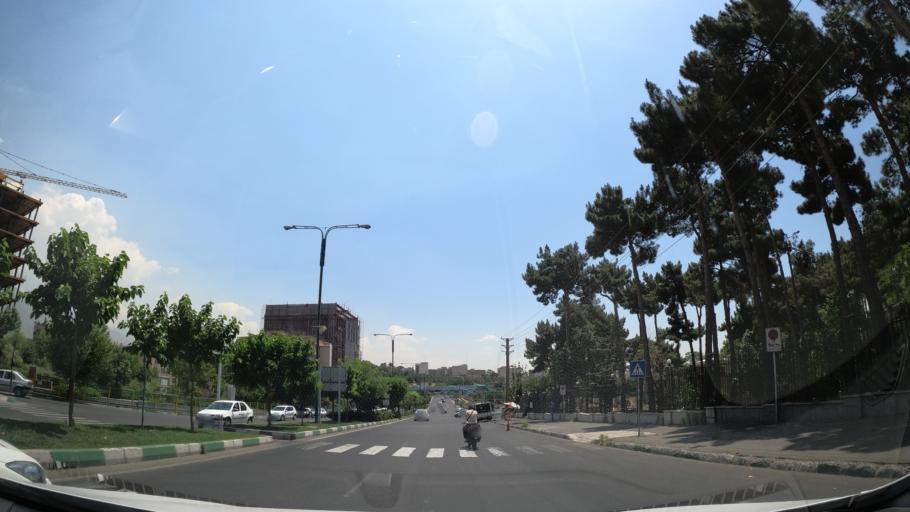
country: IR
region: Tehran
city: Tajrish
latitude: 35.7708
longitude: 51.3839
